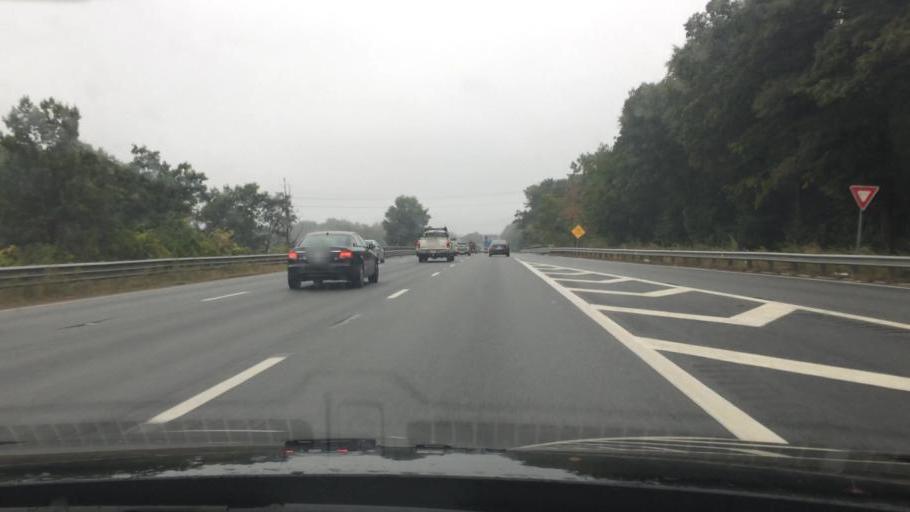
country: US
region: Massachusetts
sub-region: Middlesex County
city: Tewksbury
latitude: 42.6434
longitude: -71.2309
